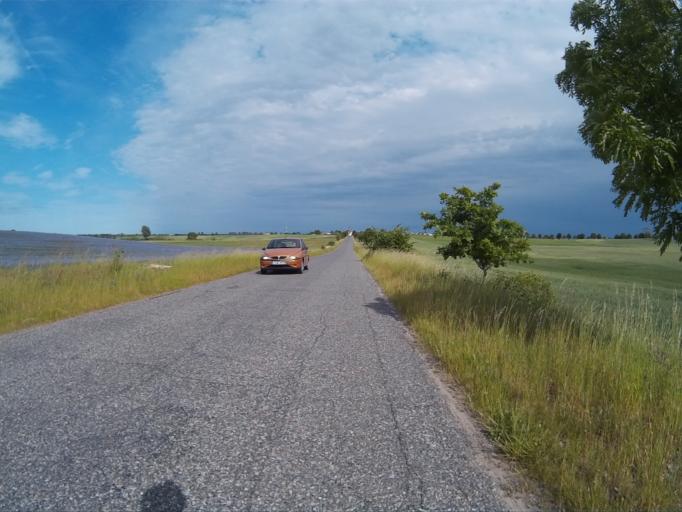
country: PL
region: Kujawsko-Pomorskie
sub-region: Powiat tucholski
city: Lubiewo
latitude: 53.4684
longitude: 18.0004
